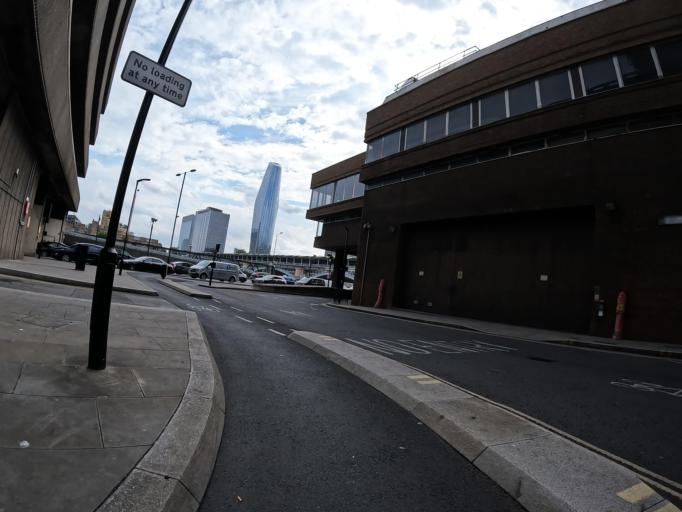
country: GB
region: England
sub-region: Greater London
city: Harringay
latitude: 51.5716
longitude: -0.0831
